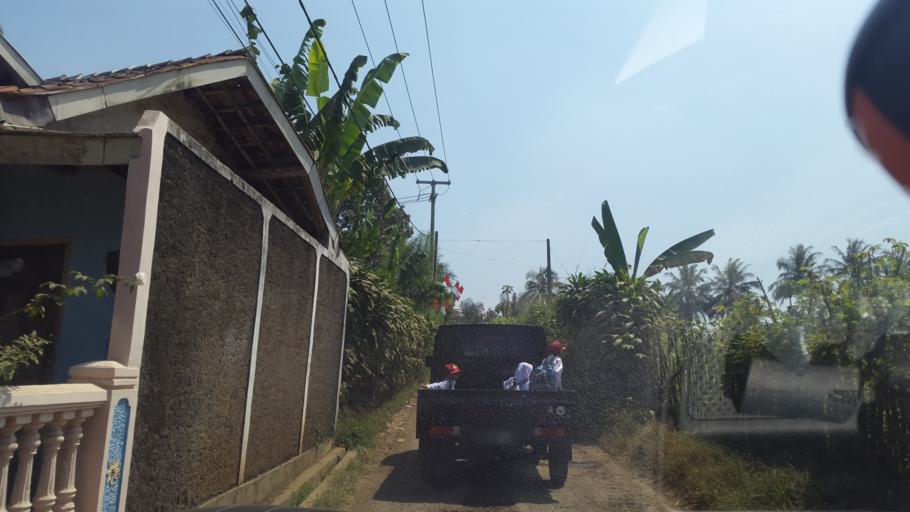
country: ID
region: West Java
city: Cicurug
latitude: -6.8577
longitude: 106.8004
